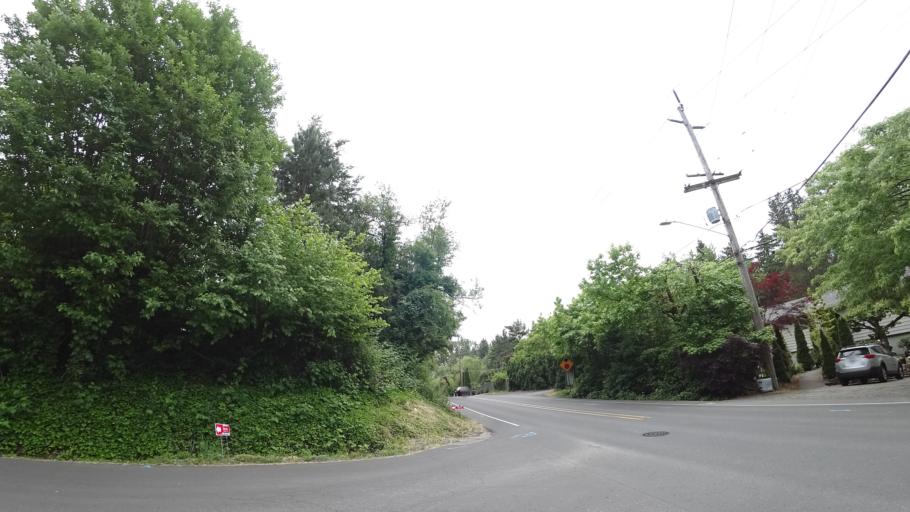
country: US
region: Oregon
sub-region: Washington County
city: Garden Home-Whitford
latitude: 45.4566
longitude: -122.7590
